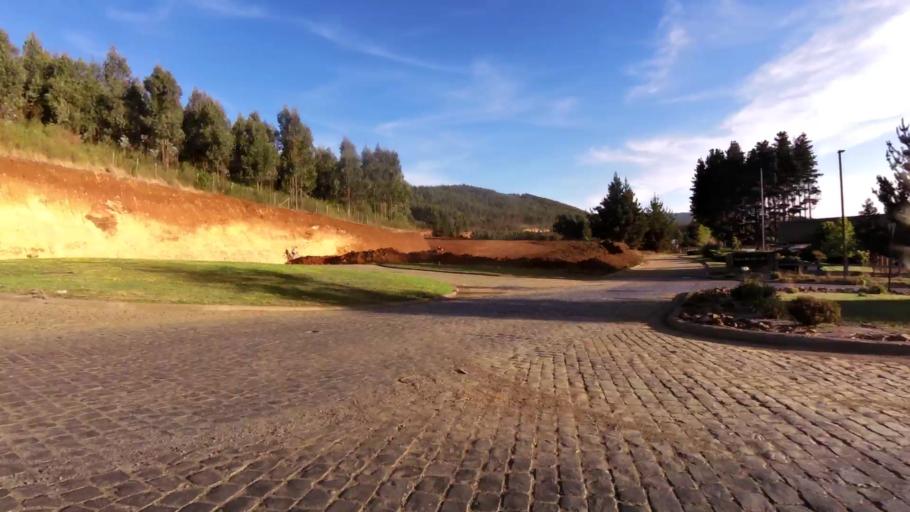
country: CL
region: Biobio
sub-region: Provincia de Concepcion
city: Concepcion
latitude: -36.8629
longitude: -73.0959
